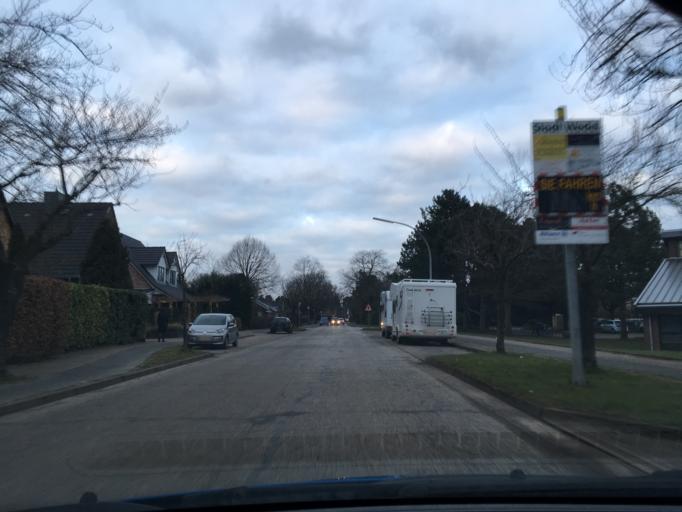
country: DE
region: Schleswig-Holstein
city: Wedel
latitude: 53.5890
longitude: 9.6987
